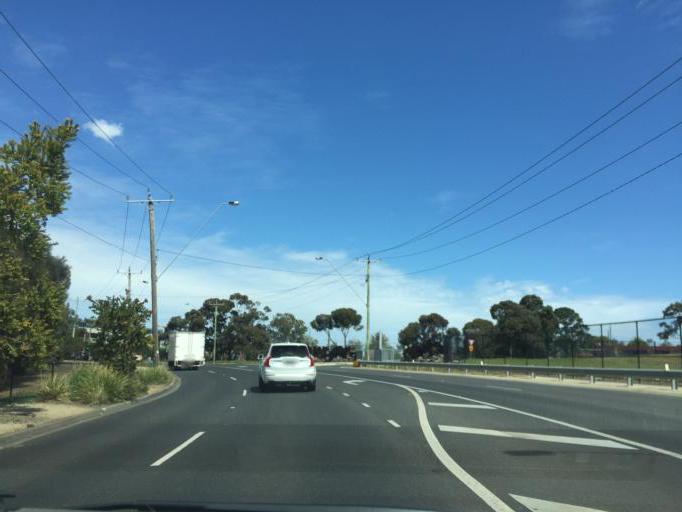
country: AU
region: Victoria
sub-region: Maribyrnong
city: Maribyrnong
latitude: -37.7785
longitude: 144.8905
